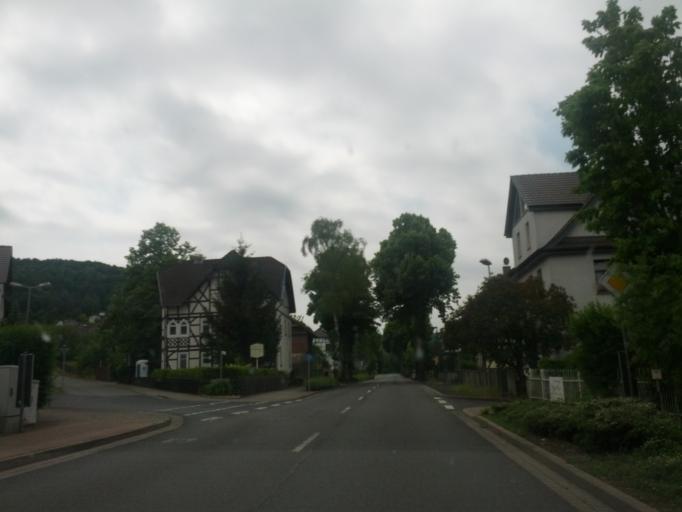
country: DE
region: Thuringia
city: Dorndorf
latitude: 50.8344
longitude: 10.0849
